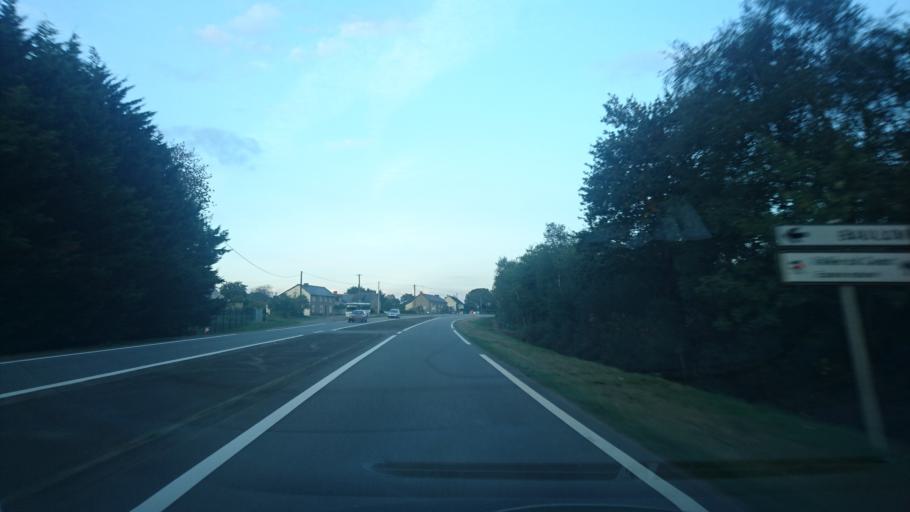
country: FR
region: Brittany
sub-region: Departement d'Ille-et-Vilaine
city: Baulon
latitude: 47.9391
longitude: -1.9280
